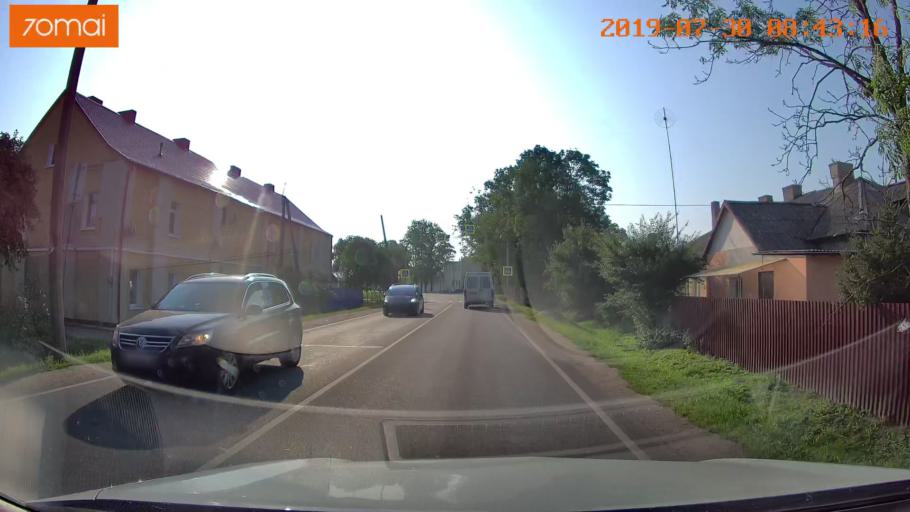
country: RU
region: Kaliningrad
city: Chernyakhovsk
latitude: 54.6272
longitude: 21.8385
